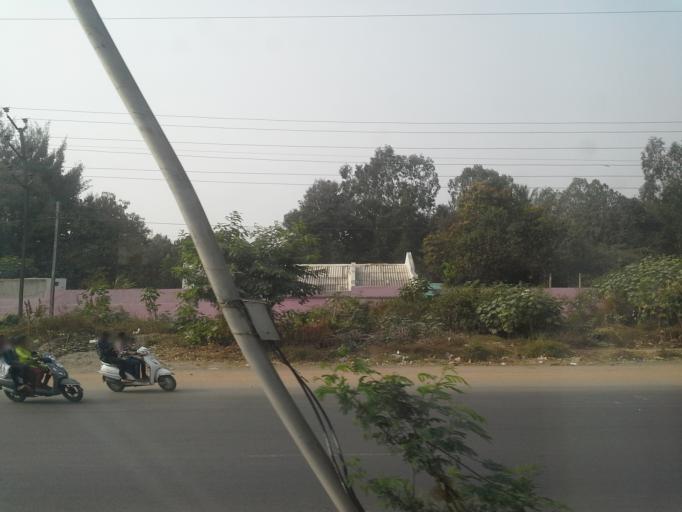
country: IN
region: Telangana
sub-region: Medak
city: Patancheru
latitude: 17.5220
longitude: 78.2750
